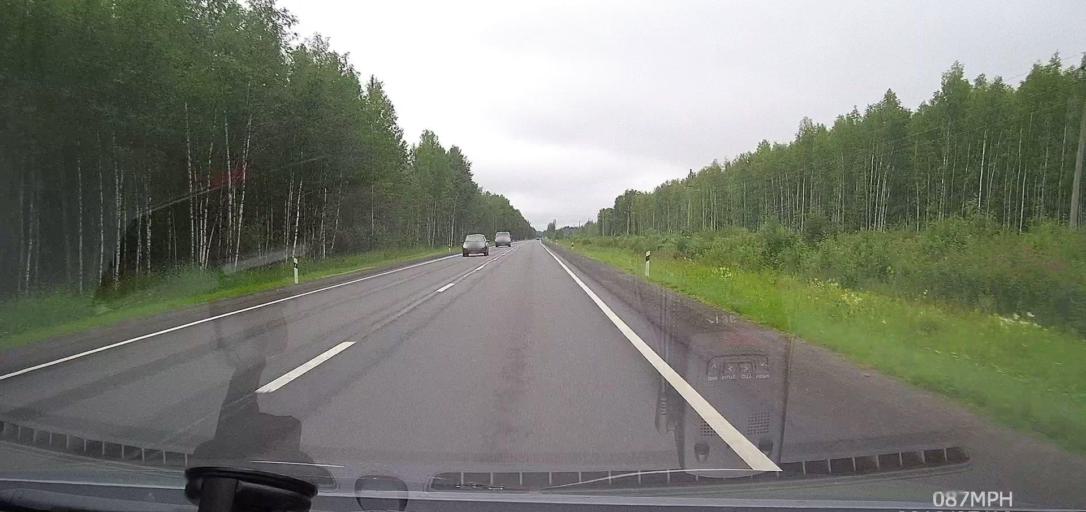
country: RU
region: Leningrad
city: Syas'stroy
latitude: 60.2240
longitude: 32.7179
